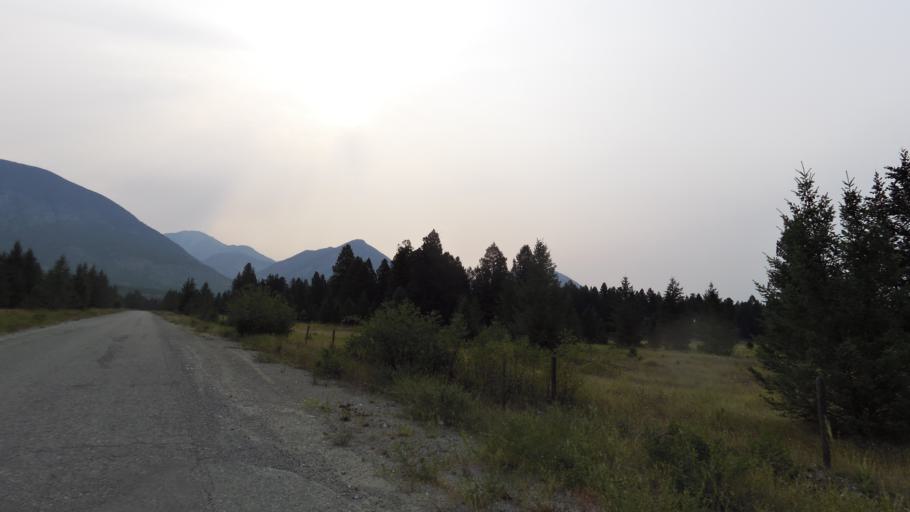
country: CA
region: British Columbia
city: Invermere
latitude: 50.5374
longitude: -116.0165
